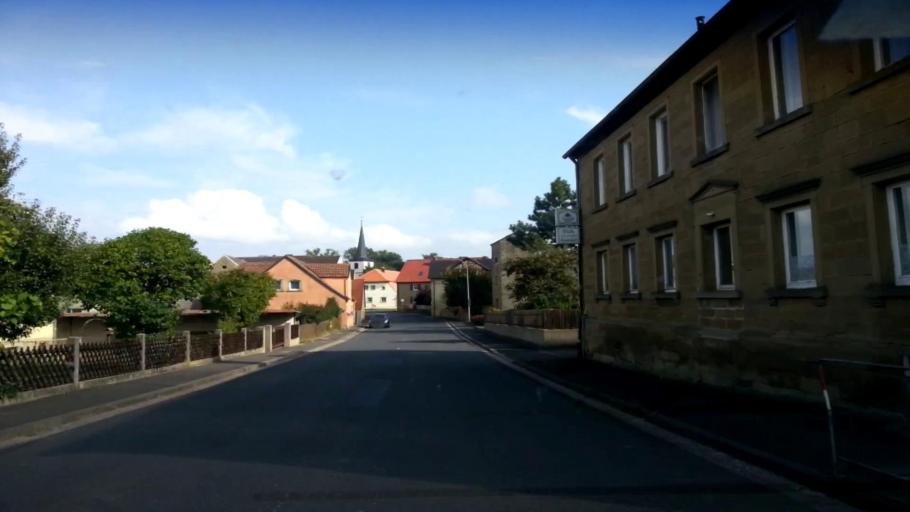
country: DE
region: Bavaria
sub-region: Regierungsbezirk Unterfranken
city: Oberschwarzach
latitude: 49.8221
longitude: 10.3962
